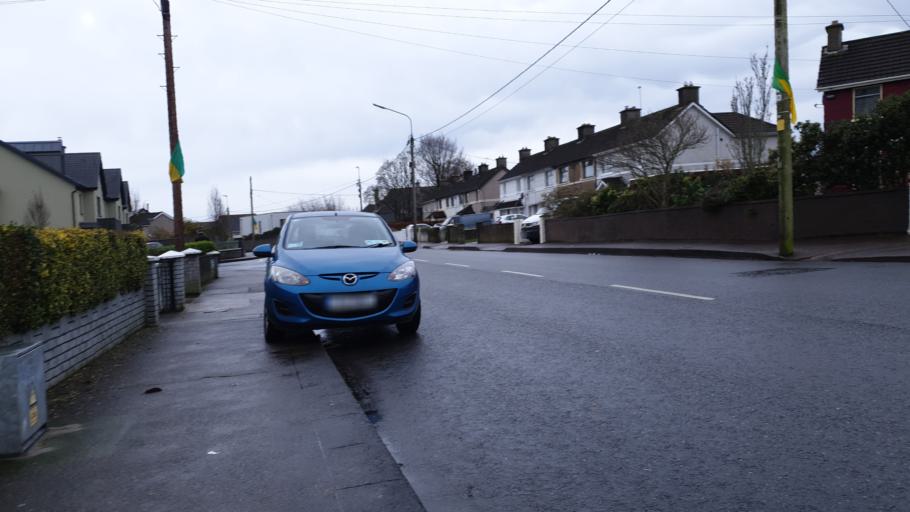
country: IE
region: Munster
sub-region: County Cork
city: Cork
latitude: 51.8914
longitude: -8.4196
